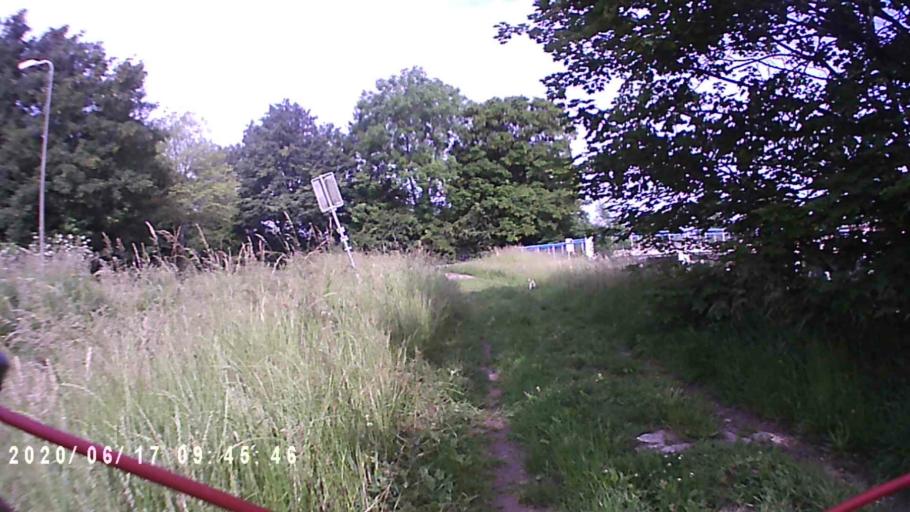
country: NL
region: Groningen
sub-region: Gemeente De Marne
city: Ulrum
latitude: 53.3538
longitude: 6.3373
